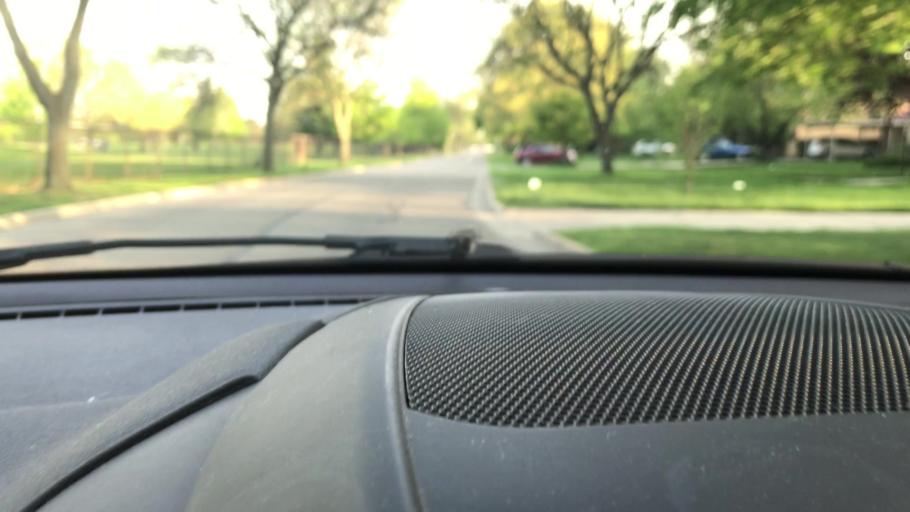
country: US
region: Michigan
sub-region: Oakland County
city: Huntington Woods
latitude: 42.4802
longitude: -83.1731
